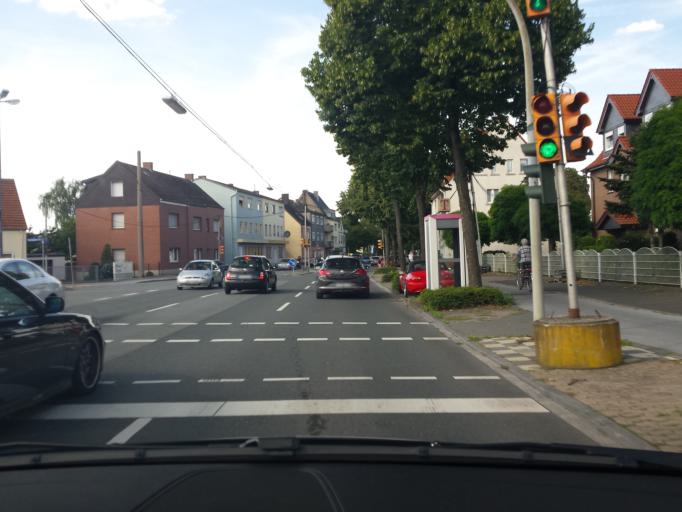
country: DE
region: North Rhine-Westphalia
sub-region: Regierungsbezirk Arnsberg
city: Lippstadt
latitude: 51.6632
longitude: 8.3441
